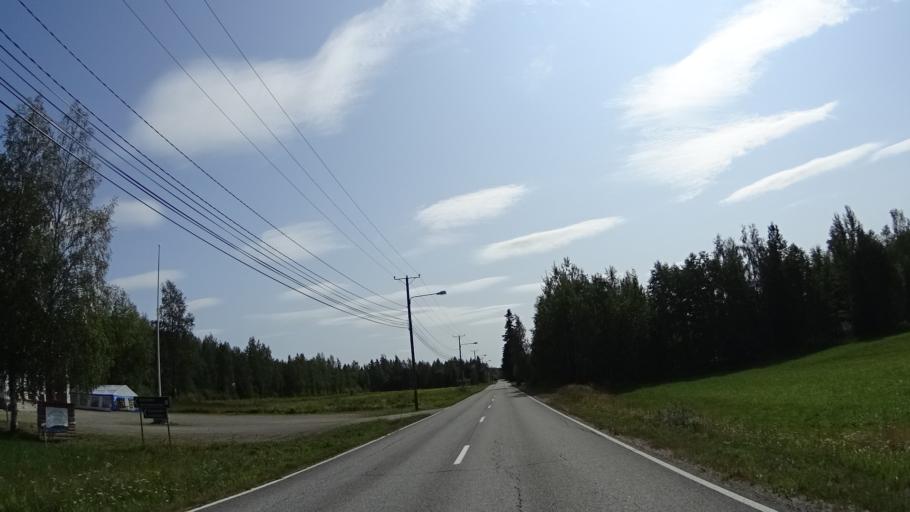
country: FI
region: Pirkanmaa
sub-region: Ylae-Pirkanmaa
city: Maenttae
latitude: 61.9165
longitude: 24.7736
